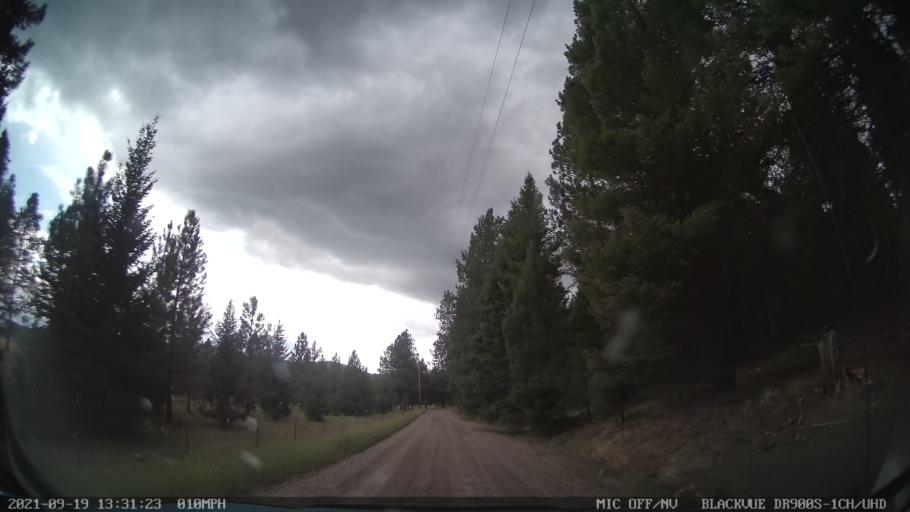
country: US
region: Montana
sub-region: Missoula County
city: Seeley Lake
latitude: 47.1209
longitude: -113.3190
